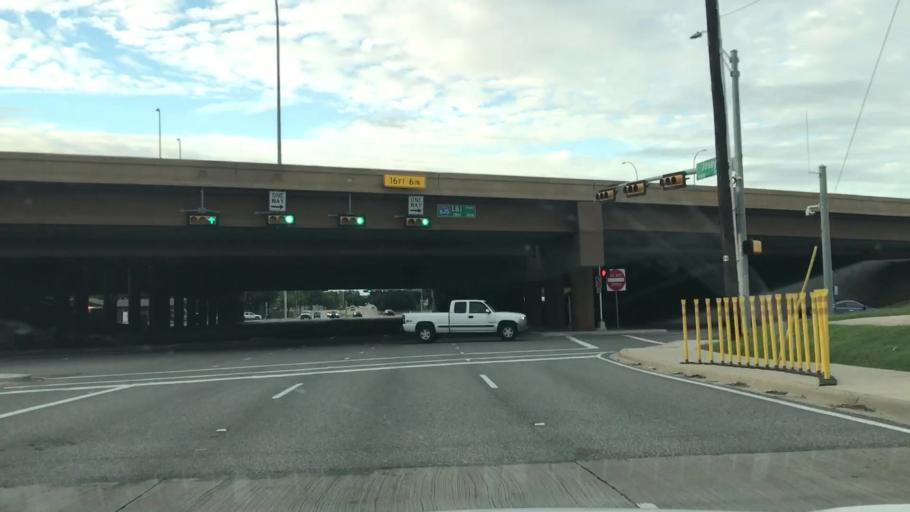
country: US
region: Texas
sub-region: Dallas County
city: Farmers Branch
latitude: 32.9102
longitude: -96.8816
